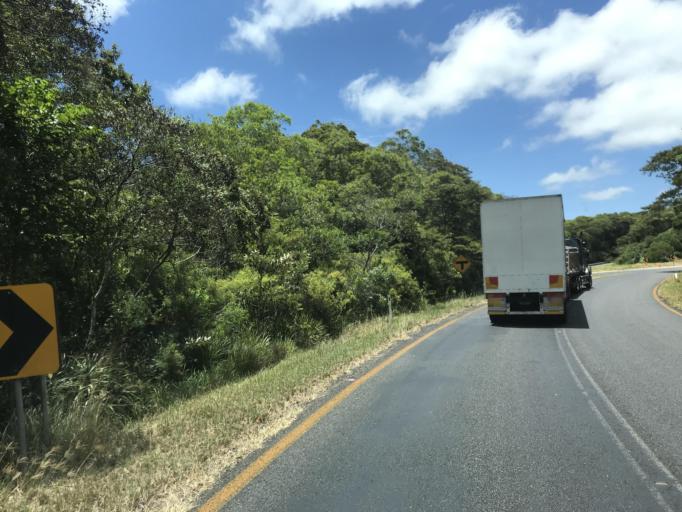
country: AU
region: Queensland
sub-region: Tablelands
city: Ravenshoe
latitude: -17.5140
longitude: 145.5137
